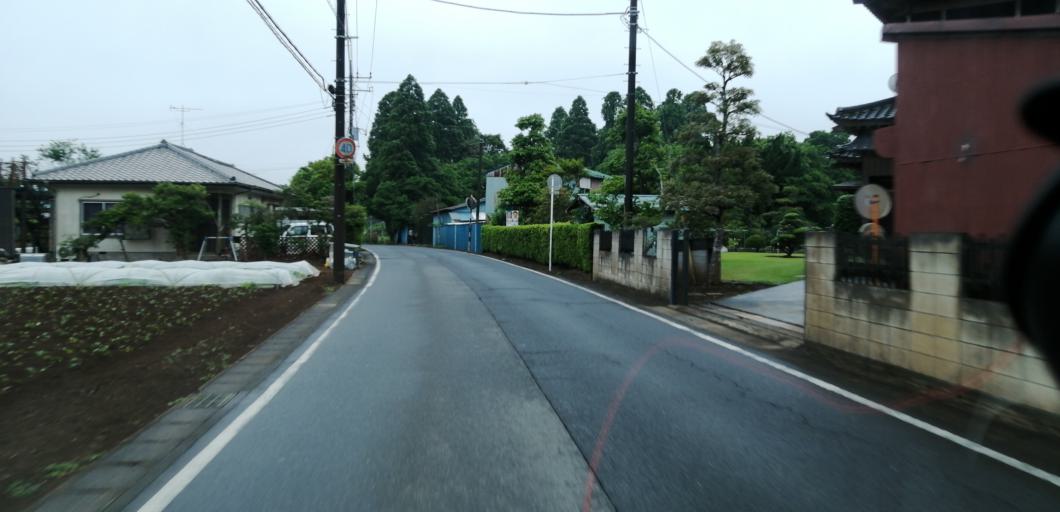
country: JP
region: Chiba
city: Oami
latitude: 35.5563
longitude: 140.2411
